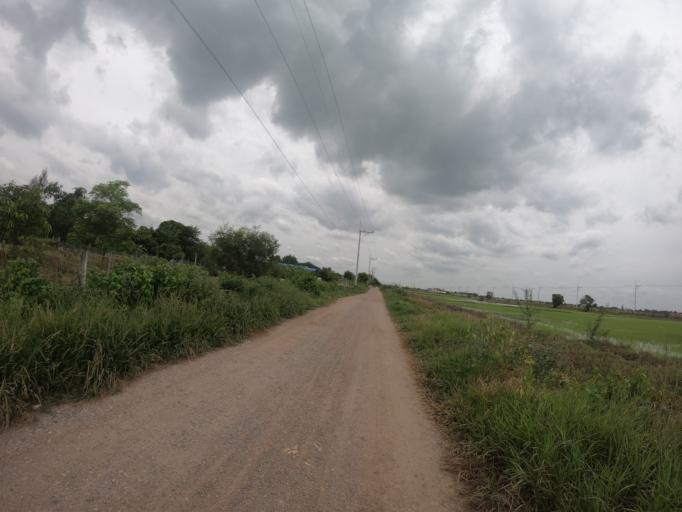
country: TH
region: Pathum Thani
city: Nong Suea
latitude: 14.0387
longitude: 100.8650
